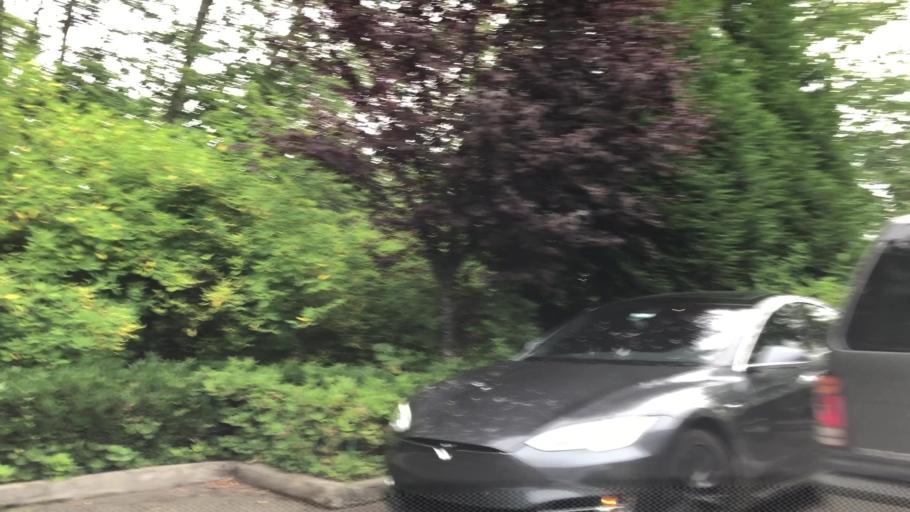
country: US
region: Washington
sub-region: Snohomish County
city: Alderwood Manor
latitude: 47.8190
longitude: -122.2739
